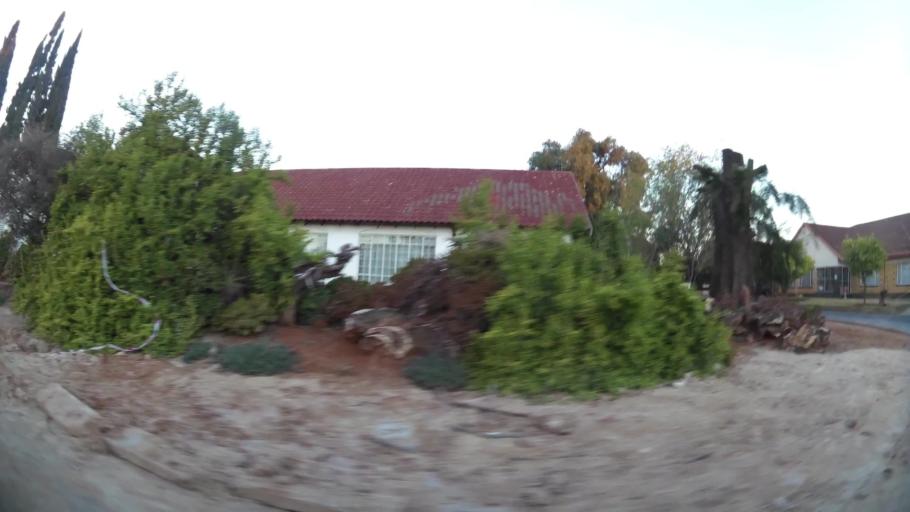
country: ZA
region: Northern Cape
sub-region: Frances Baard District Municipality
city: Kimberley
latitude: -28.7214
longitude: 24.7749
